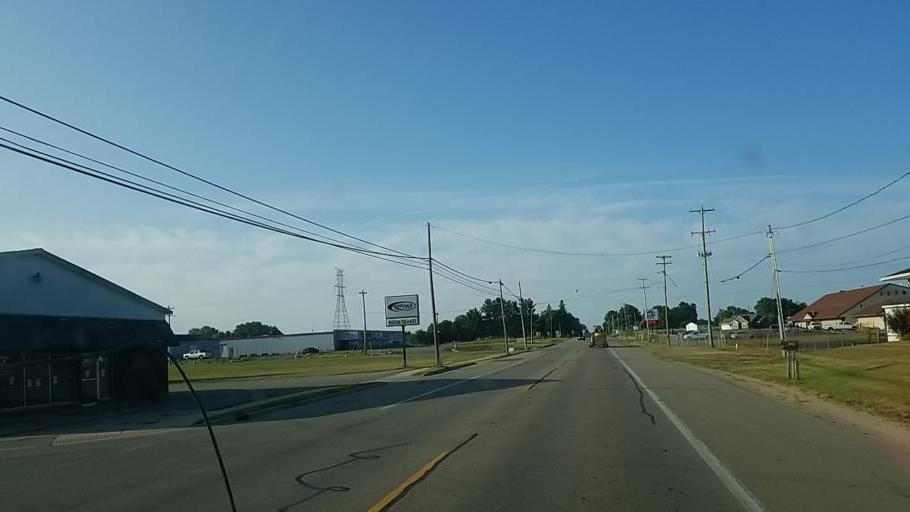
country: US
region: Michigan
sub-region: Montcalm County
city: Stanton
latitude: 43.2073
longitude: -85.0737
